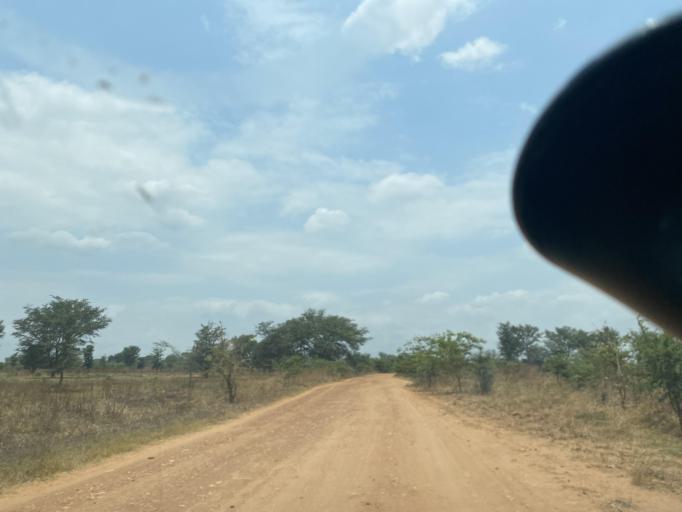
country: ZM
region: Lusaka
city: Chongwe
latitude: -15.5188
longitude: 28.8210
